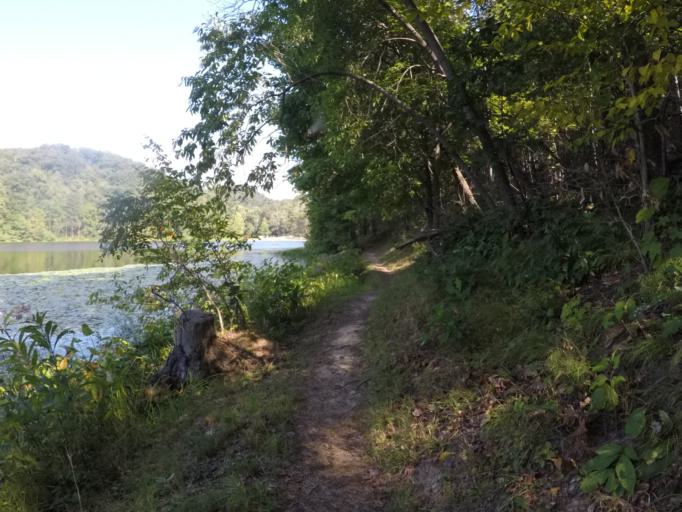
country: US
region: Ohio
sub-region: Lawrence County
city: Ironton
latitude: 38.6172
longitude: -82.6269
